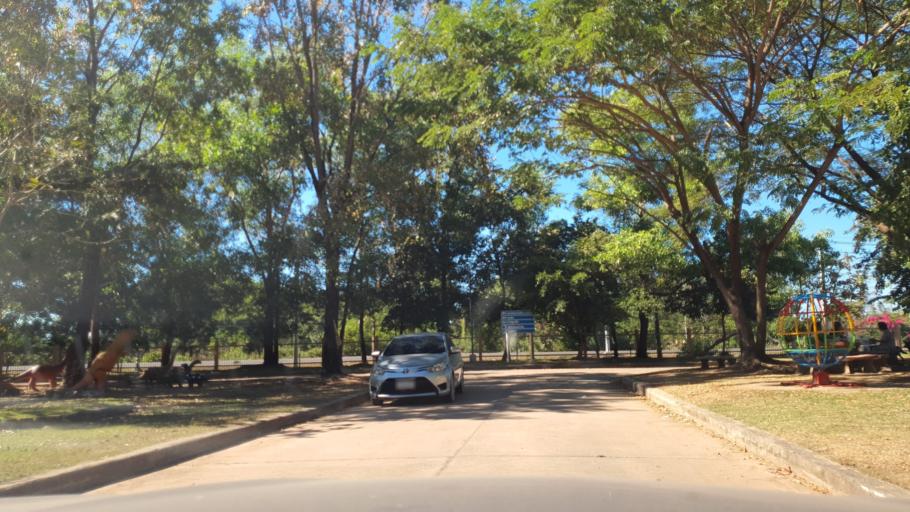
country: TH
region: Nakhon Phanom
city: Nakhon Phanom
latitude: 17.3738
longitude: 104.7363
